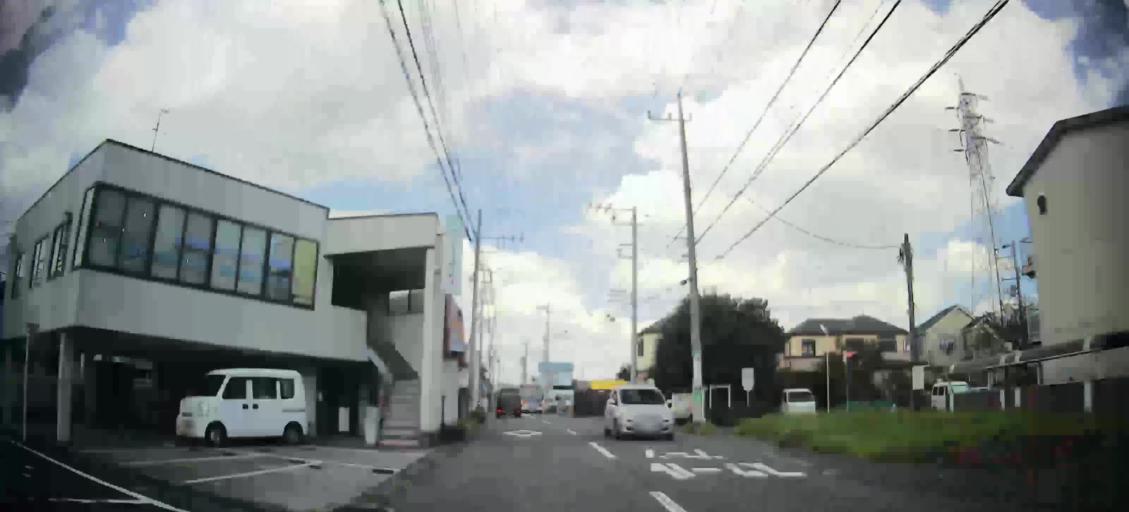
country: JP
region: Kanagawa
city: Yokohama
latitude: 35.4654
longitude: 139.5604
